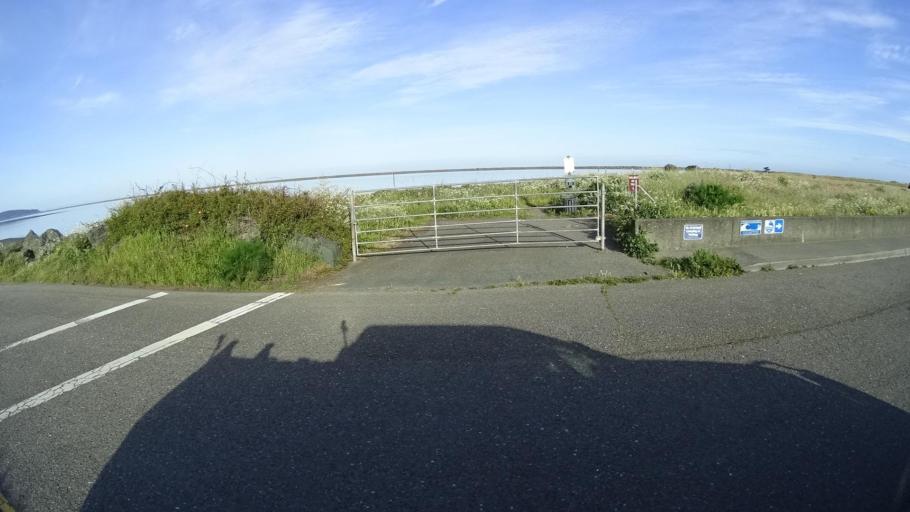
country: US
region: California
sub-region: Humboldt County
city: Humboldt Hill
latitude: 40.7375
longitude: -124.2202
